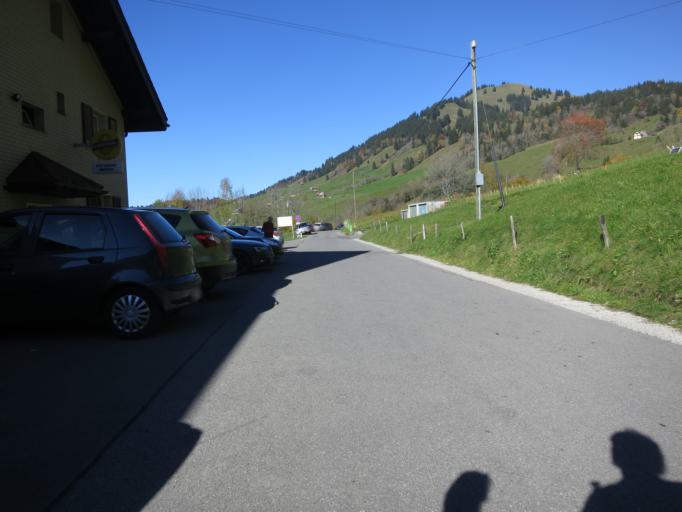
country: CH
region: Schwyz
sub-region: Bezirk March
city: Vorderthal
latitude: 47.0897
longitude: 8.9306
